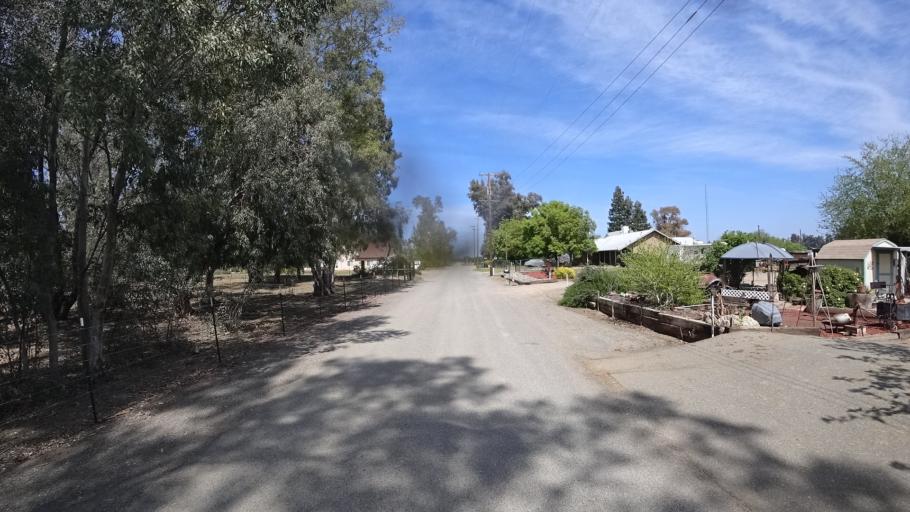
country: US
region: California
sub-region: Glenn County
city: Willows
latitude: 39.5884
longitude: -122.2015
